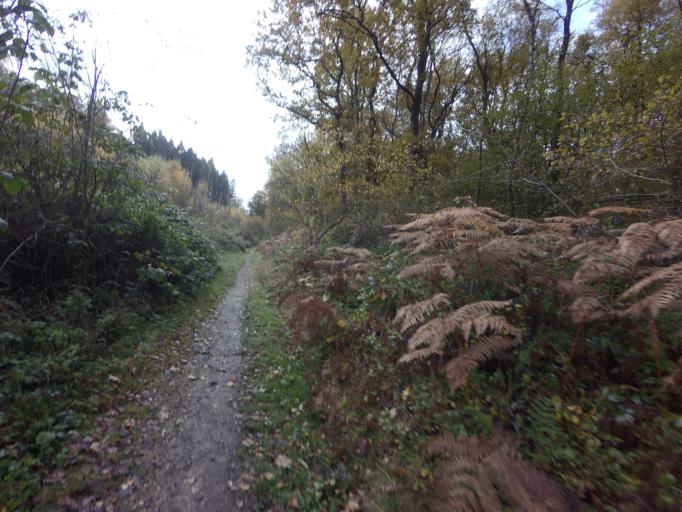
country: BE
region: Flanders
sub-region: Provincie Limburg
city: Sint-Pieters-Voeren
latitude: 50.7781
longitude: 5.8854
